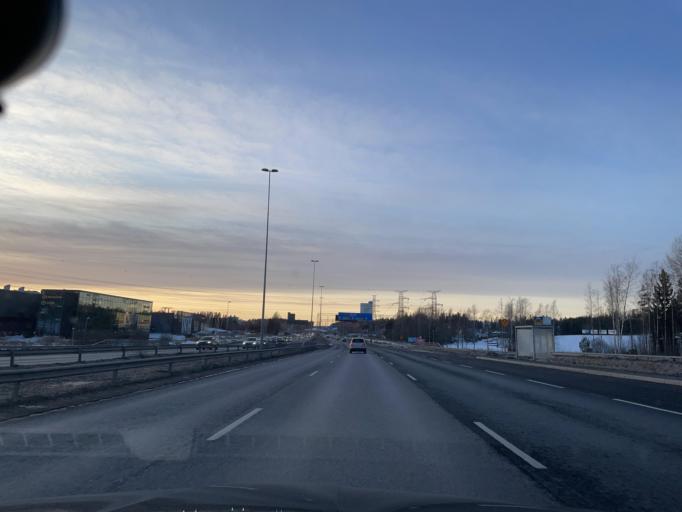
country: FI
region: Uusimaa
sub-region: Helsinki
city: Teekkarikylae
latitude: 60.2995
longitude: 24.9011
